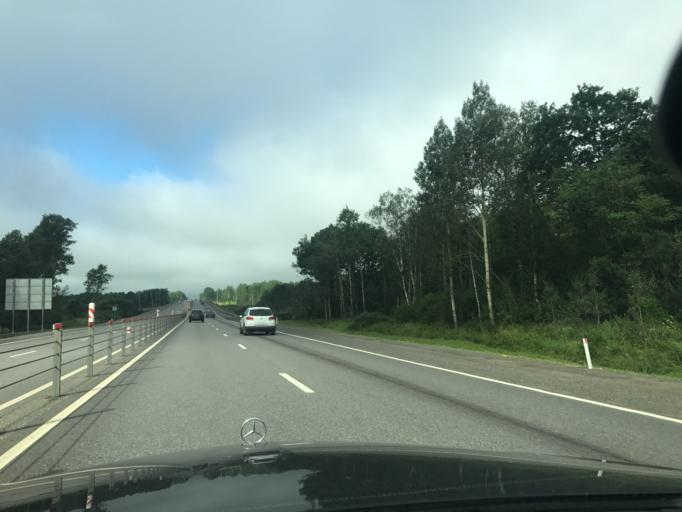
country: RU
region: Smolensk
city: Vyaz'ma
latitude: 55.2635
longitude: 34.3828
